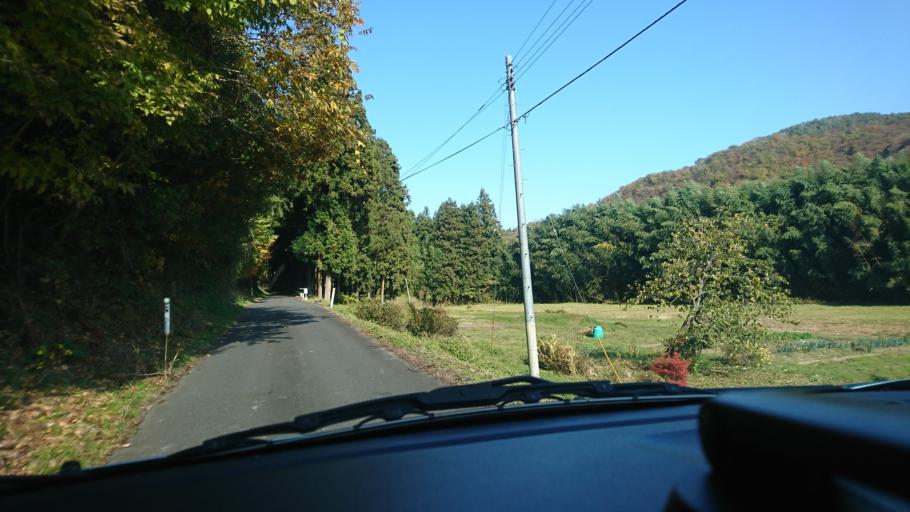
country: JP
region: Iwate
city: Ichinoseki
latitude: 38.8185
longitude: 141.2507
